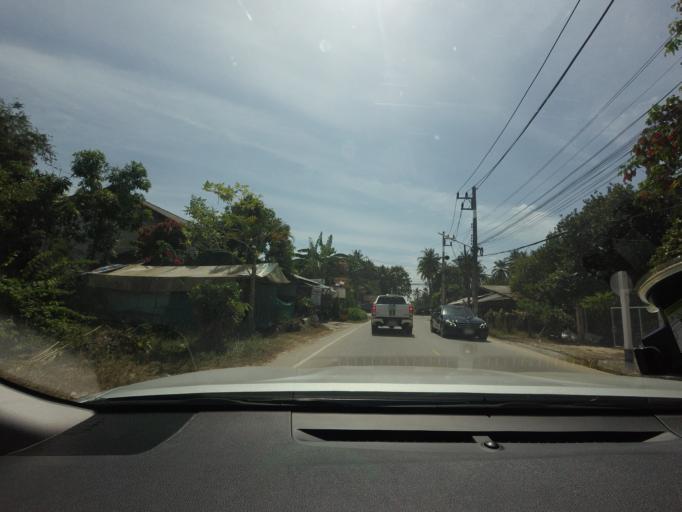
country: TH
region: Narathiwat
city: Narathiwat
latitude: 6.4431
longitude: 101.7977
